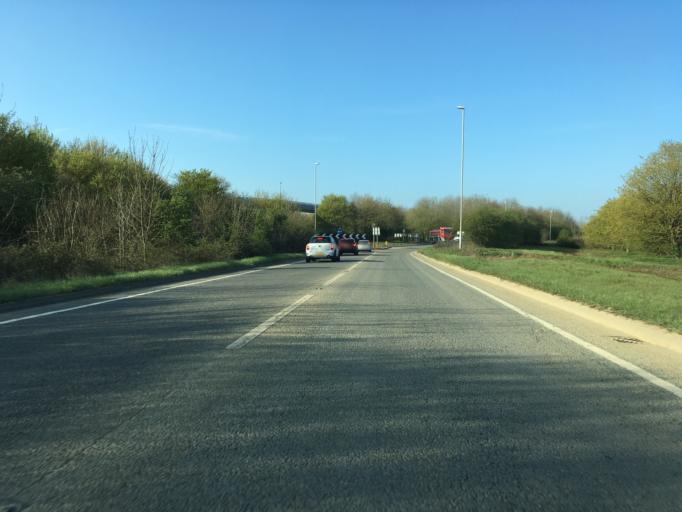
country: GB
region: England
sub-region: Northamptonshire
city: Deanshanger
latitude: 52.0520
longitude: -0.8728
